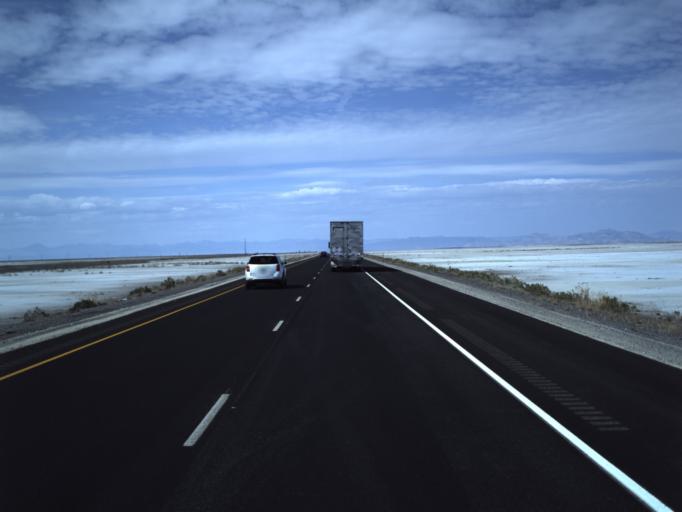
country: US
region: Utah
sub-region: Tooele County
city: Wendover
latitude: 40.7319
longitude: -113.5021
